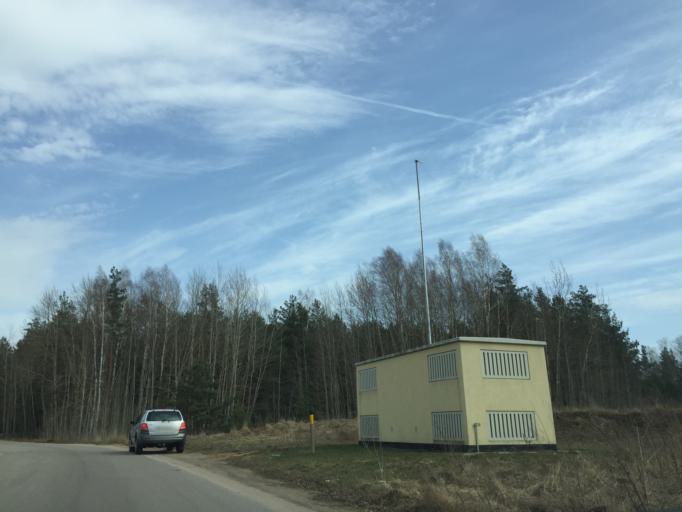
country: LV
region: Daugavpils
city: Daugavpils
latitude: 55.8995
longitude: 26.4667
